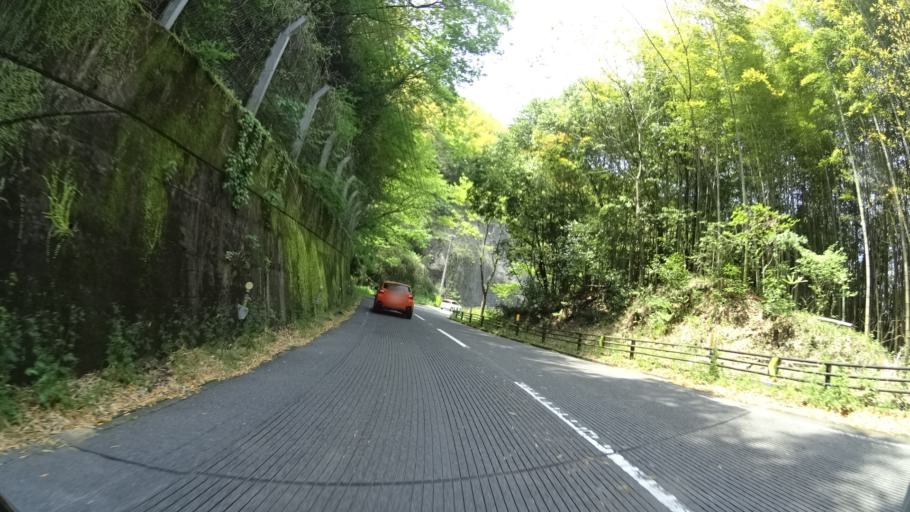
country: JP
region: Ehime
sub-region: Shikoku-chuo Shi
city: Matsuyama
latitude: 33.8775
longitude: 132.8360
